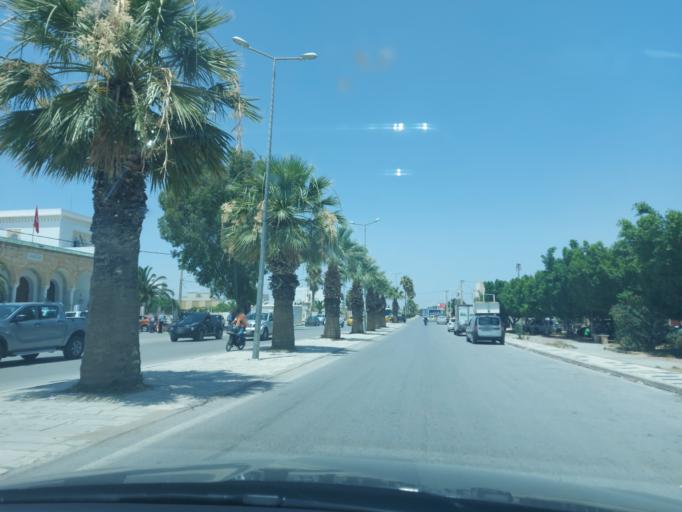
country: TN
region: Silyanah
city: Siliana
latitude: 36.0908
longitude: 9.3719
